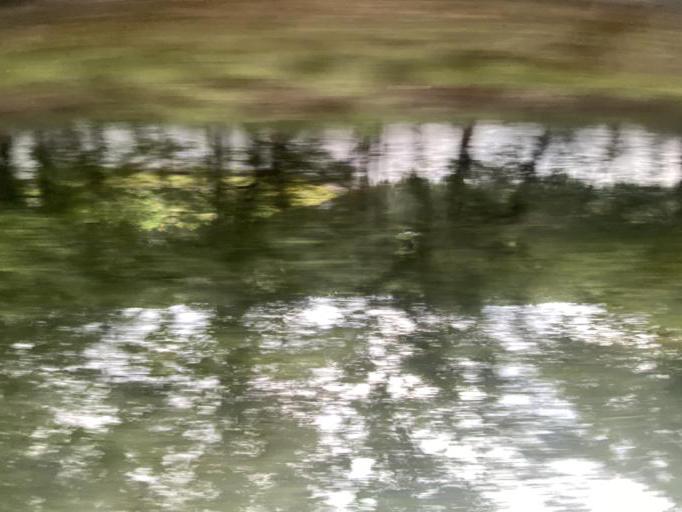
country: US
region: West Virginia
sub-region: Mineral County
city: Fort Ashby
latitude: 39.5230
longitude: -78.5319
